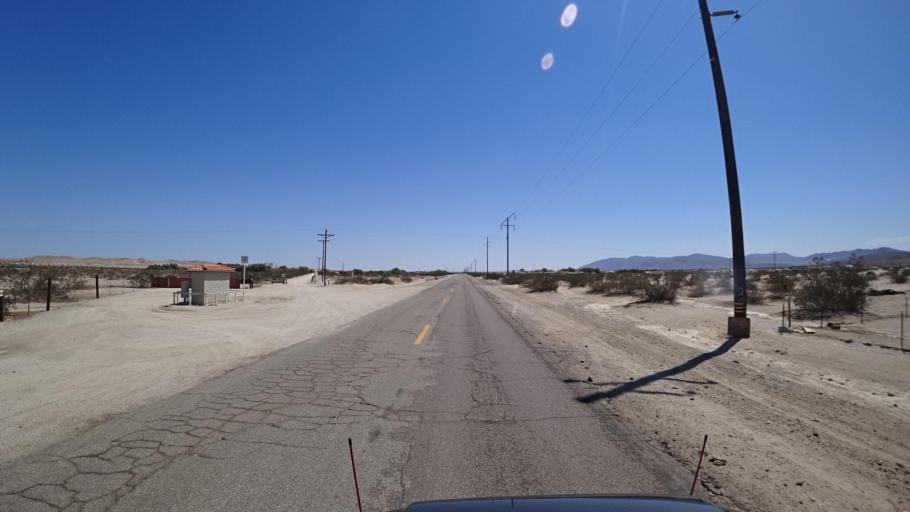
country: US
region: California
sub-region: Imperial County
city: Salton City
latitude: 33.1040
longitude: -116.1250
